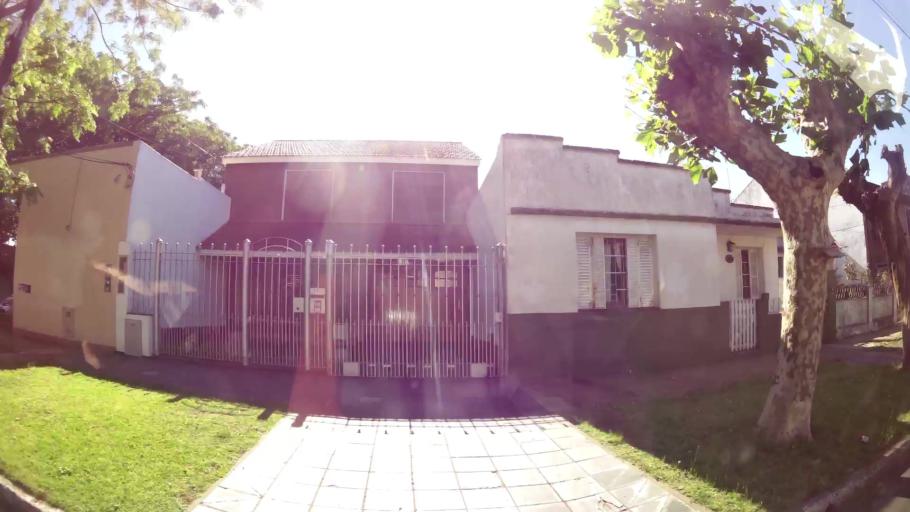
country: AR
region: Buenos Aires
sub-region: Partido de Lomas de Zamora
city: Lomas de Zamora
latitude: -34.7606
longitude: -58.4163
